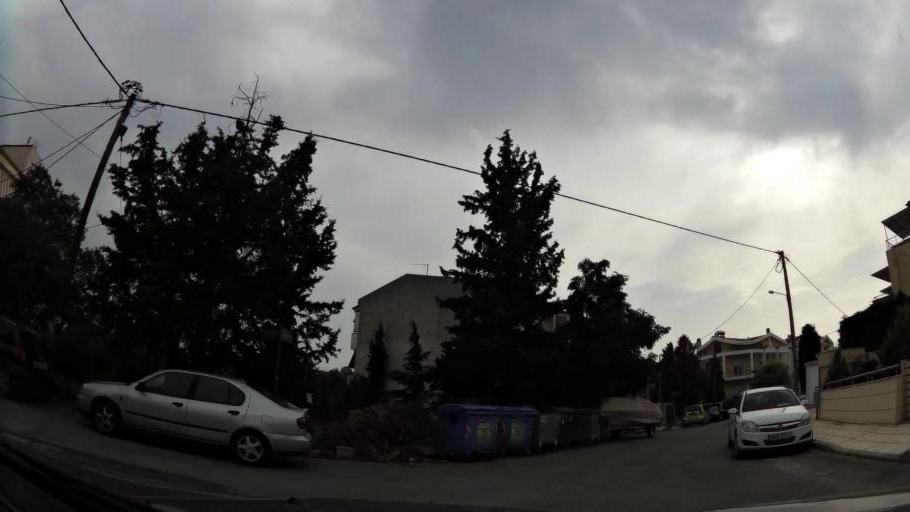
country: GR
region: Central Macedonia
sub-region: Nomos Thessalonikis
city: Oraiokastro
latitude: 40.7116
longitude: 22.9316
